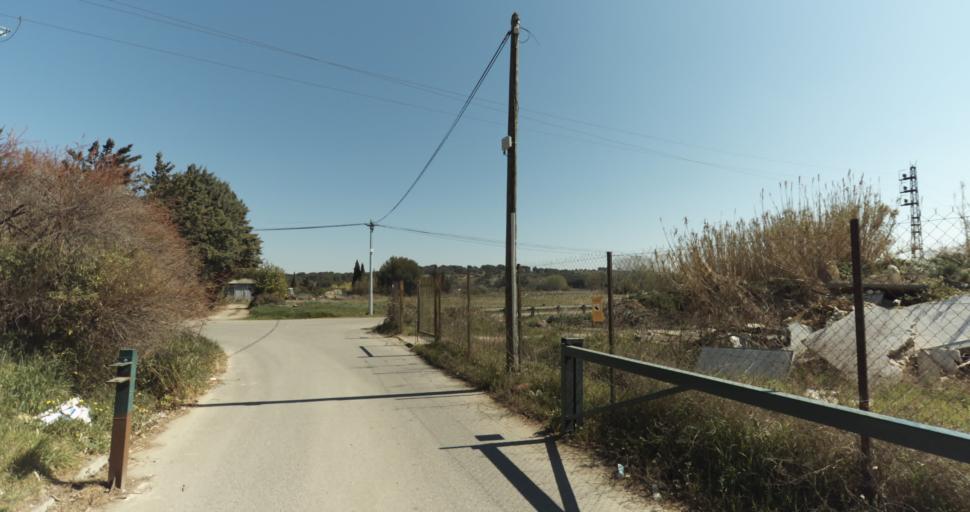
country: FR
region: Provence-Alpes-Cote d'Azur
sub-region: Departement des Bouches-du-Rhone
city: Pelissanne
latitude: 43.6195
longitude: 5.1600
